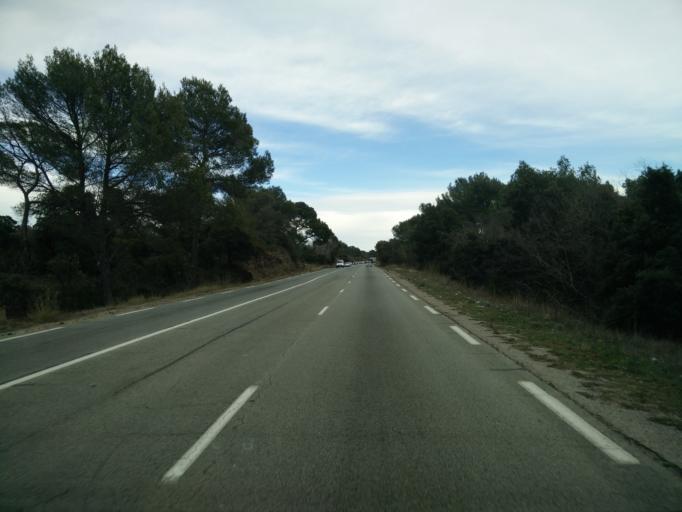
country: FR
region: Provence-Alpes-Cote d'Azur
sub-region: Departement du Var
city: Roquebrune-sur-Argens
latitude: 43.4666
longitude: 6.6143
